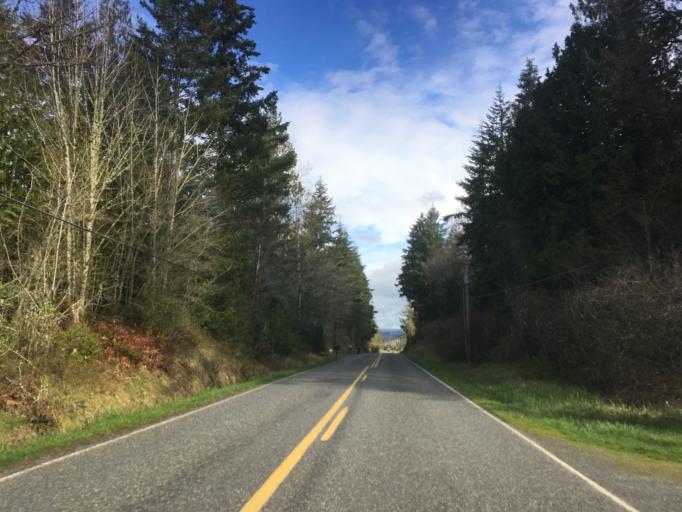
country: US
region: Washington
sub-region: Whatcom County
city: Sudden Valley
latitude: 48.7977
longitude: -122.3439
